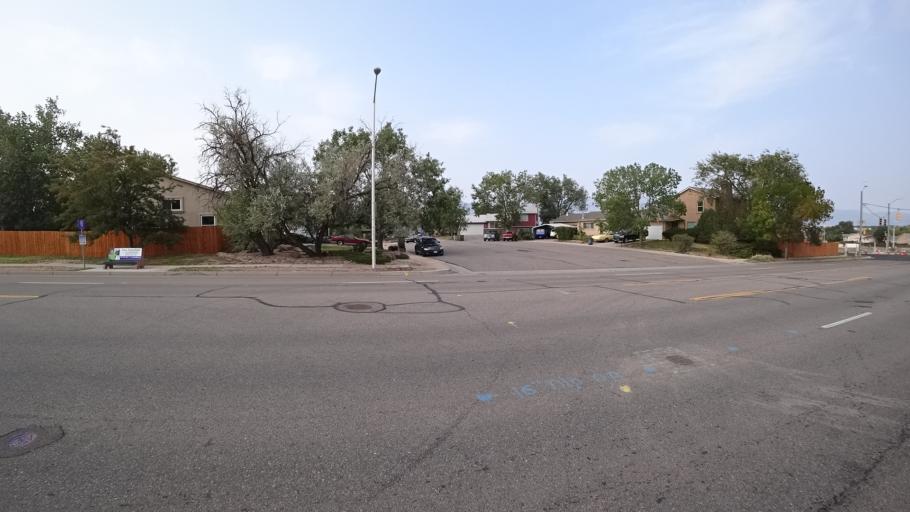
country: US
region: Colorado
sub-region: El Paso County
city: Stratmoor
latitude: 38.8040
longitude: -104.7449
